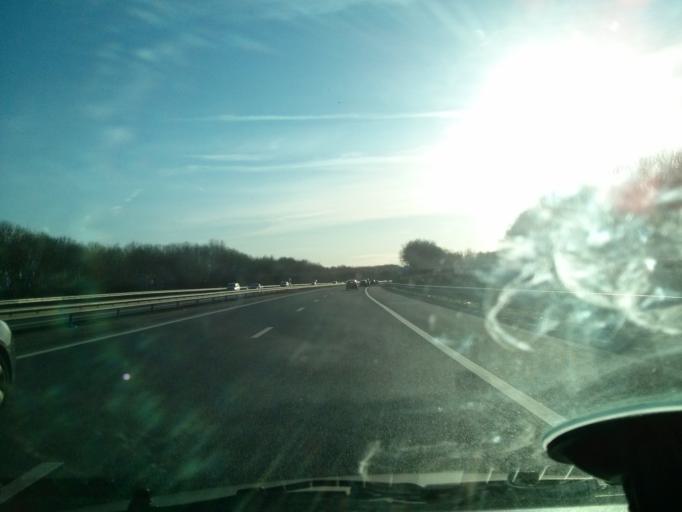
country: NL
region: North Brabant
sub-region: Gemeente Landerd
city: Reek
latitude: 51.7922
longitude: 5.6607
